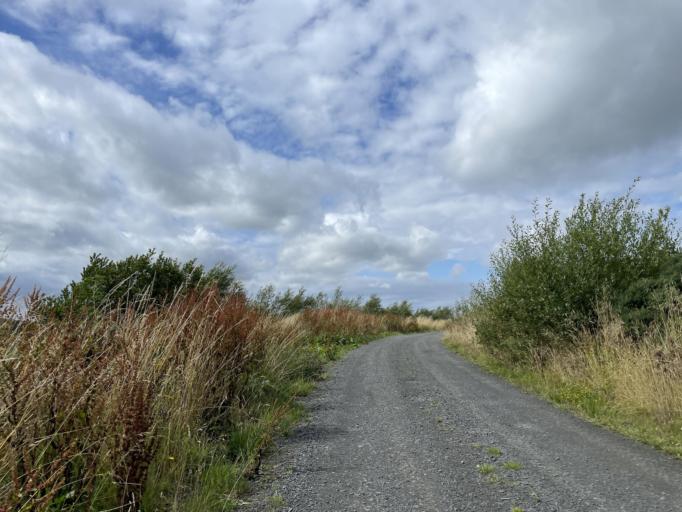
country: GB
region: Scotland
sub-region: South Ayrshire
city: Maybole
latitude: 55.2078
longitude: -4.6784
